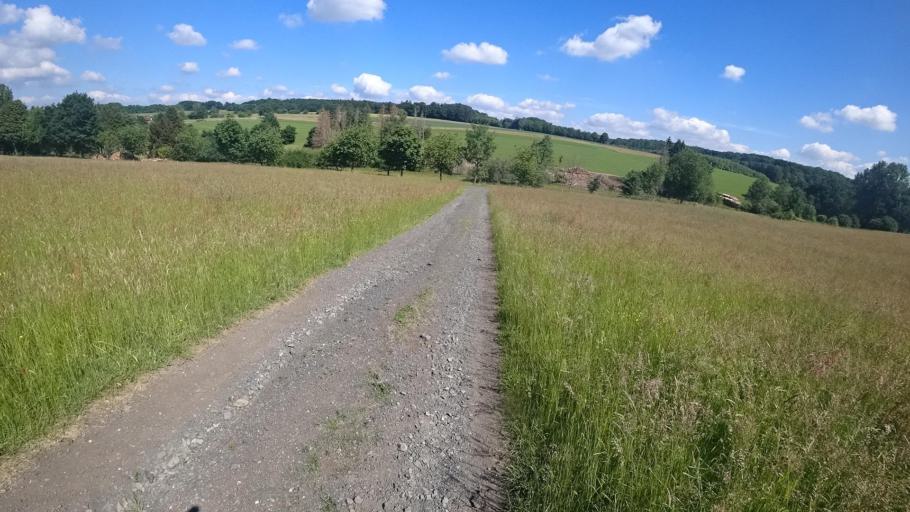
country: DE
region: Rheinland-Pfalz
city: Sorth
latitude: 50.6960
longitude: 7.6936
